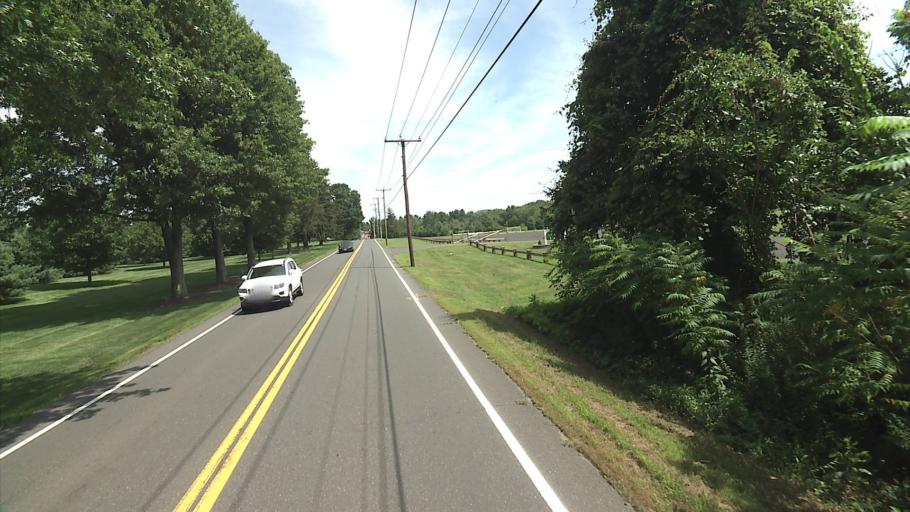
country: US
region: Connecticut
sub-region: Tolland County
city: Ellington
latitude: 41.8753
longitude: -72.4869
